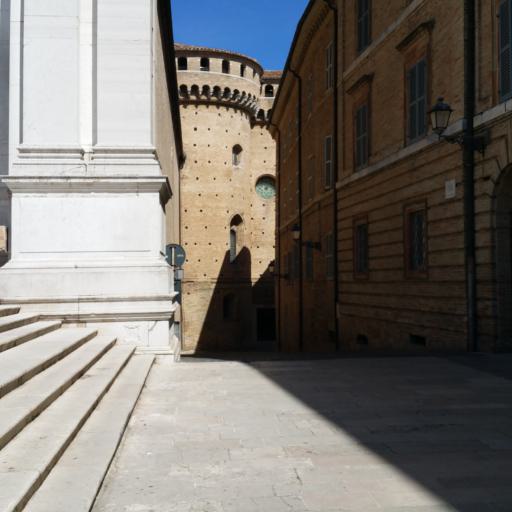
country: IT
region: The Marches
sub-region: Provincia di Ancona
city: Loreto
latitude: 43.4409
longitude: 13.6100
